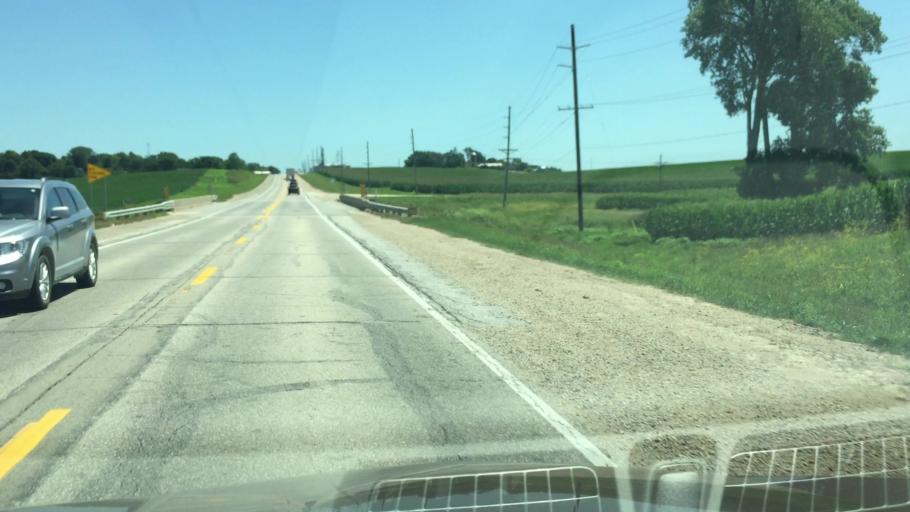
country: US
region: Iowa
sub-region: Cedar County
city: Mechanicsville
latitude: 41.8884
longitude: -91.1638
